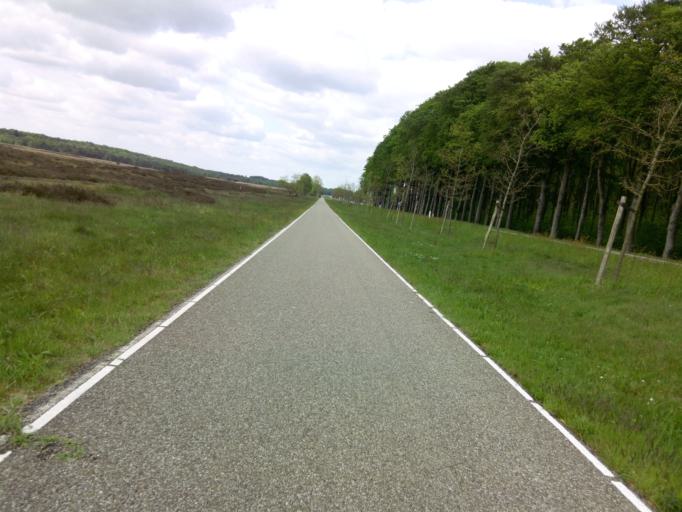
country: NL
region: Gelderland
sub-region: Gemeente Renkum
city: Heelsum
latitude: 52.0373
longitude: 5.7317
